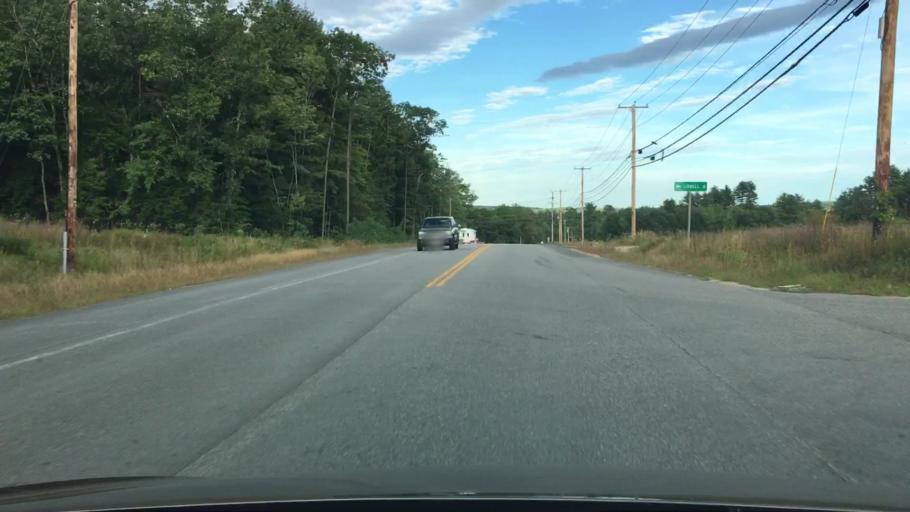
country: US
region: Maine
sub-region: Oxford County
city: Lovell
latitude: 44.0651
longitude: -70.8217
